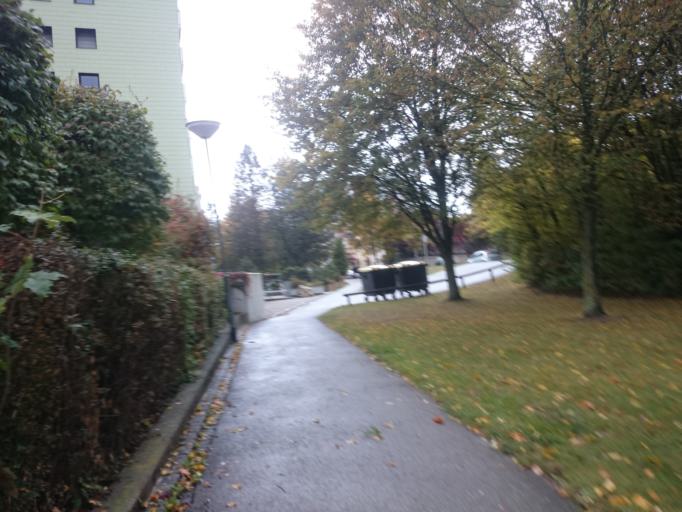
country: DE
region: Bavaria
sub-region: Swabia
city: Gersthofen
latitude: 48.4298
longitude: 10.8687
